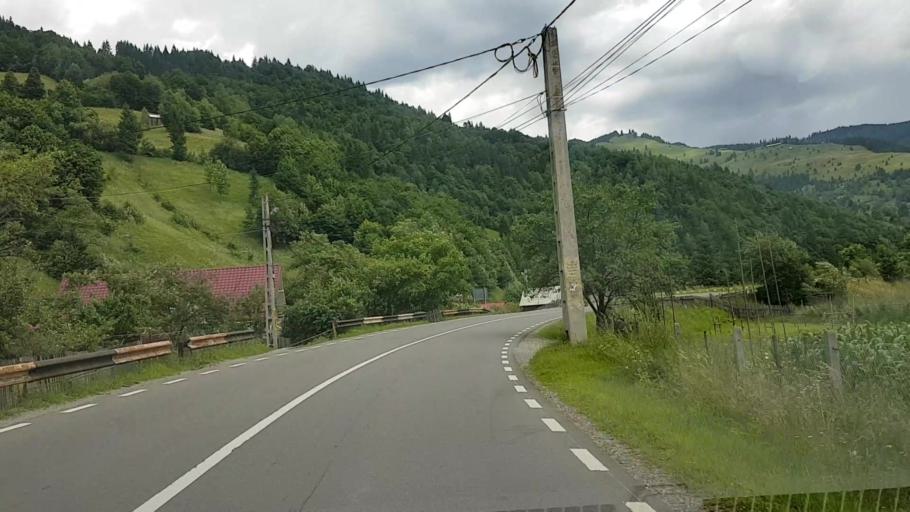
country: RO
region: Neamt
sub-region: Comuna Farcasa
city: Farcasa
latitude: 47.1518
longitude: 25.8513
